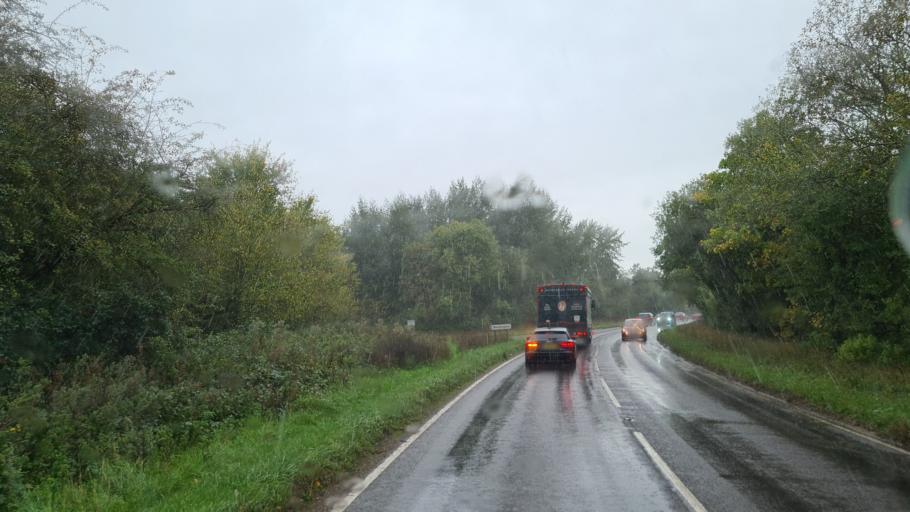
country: GB
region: England
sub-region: West Sussex
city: Washington
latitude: 50.9060
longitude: -0.4023
